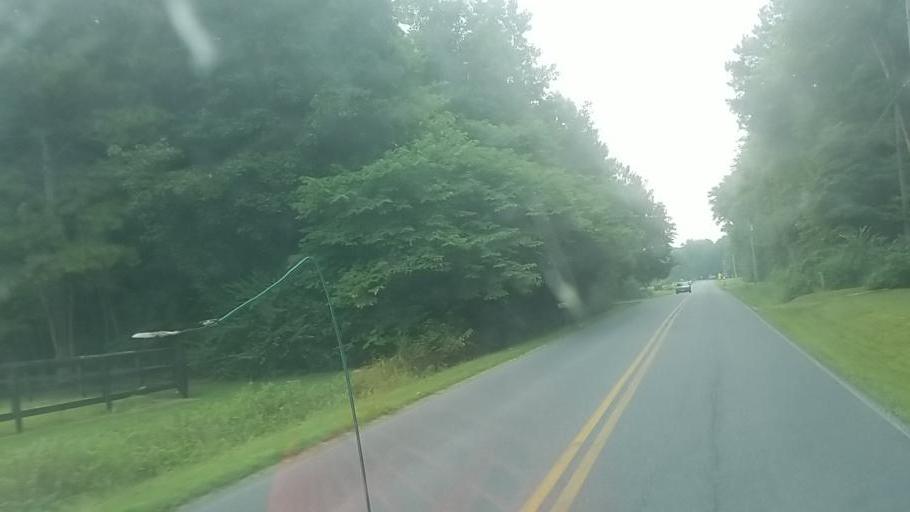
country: US
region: Maryland
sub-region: Wicomico County
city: Delmar
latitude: 38.4134
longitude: -75.5152
